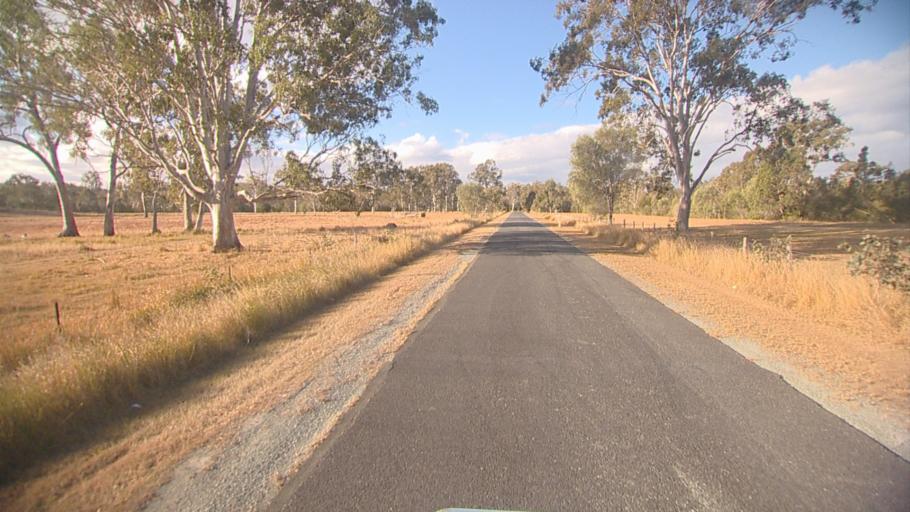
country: AU
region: Queensland
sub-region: Logan
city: Cedar Vale
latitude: -27.8874
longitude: 153.0728
